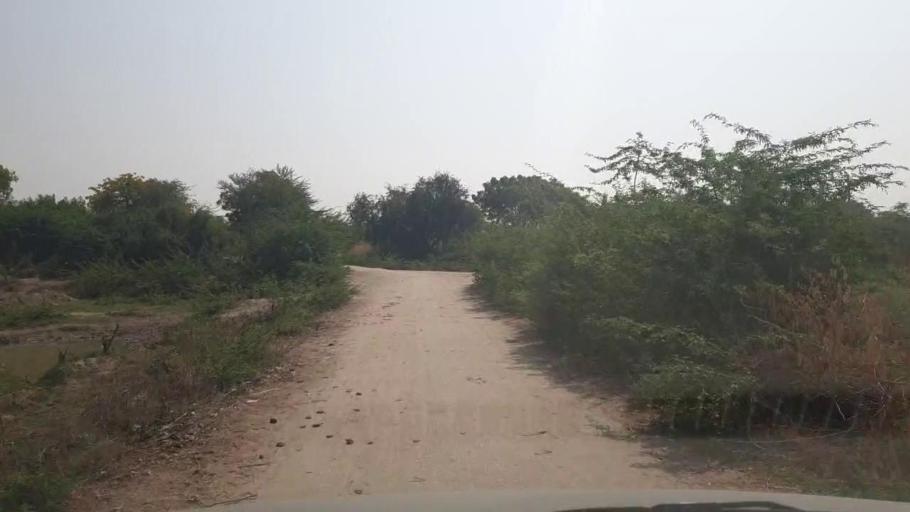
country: PK
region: Sindh
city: Chor
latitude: 25.4403
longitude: 69.7500
